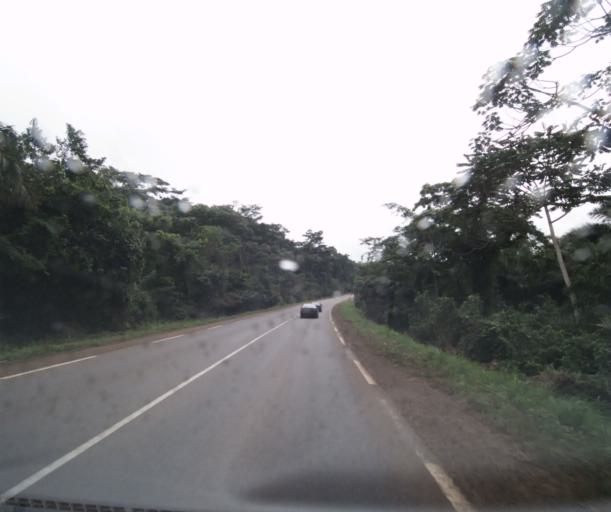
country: CM
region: Centre
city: Mbankomo
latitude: 3.7821
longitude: 11.2503
